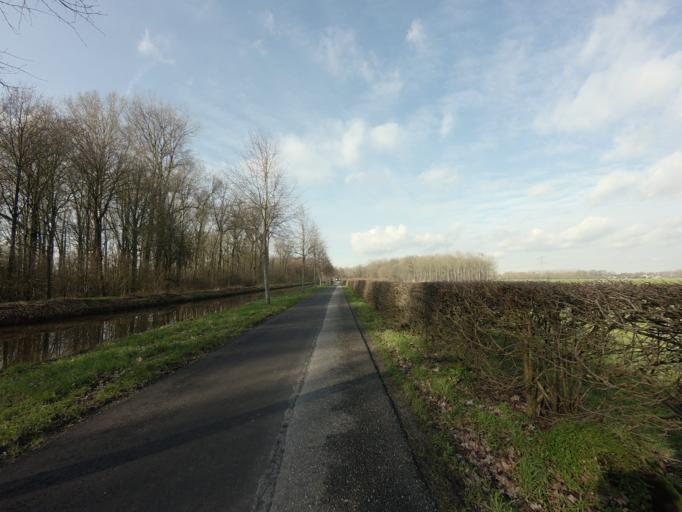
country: NL
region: Utrecht
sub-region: Gemeente Woerden
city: Woerden
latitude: 52.0611
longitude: 4.9021
